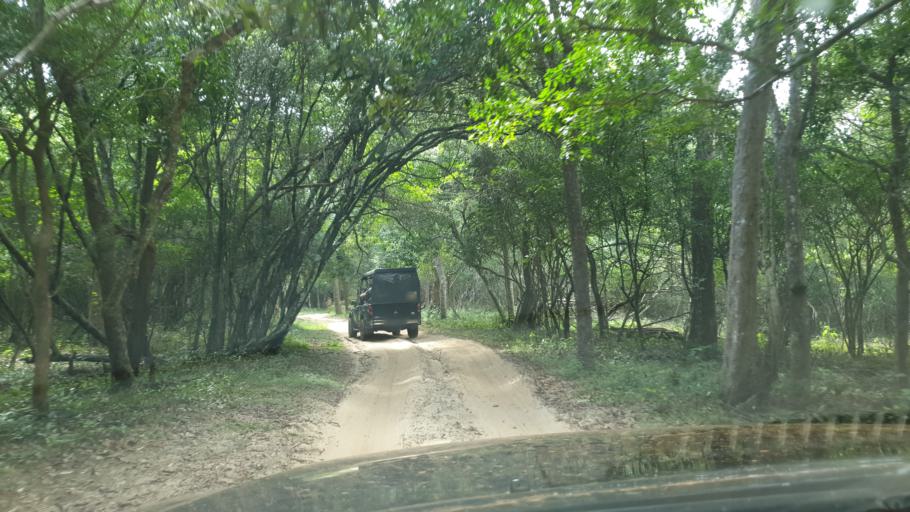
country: LK
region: North Western
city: Puttalam
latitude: 8.4133
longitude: 79.9916
